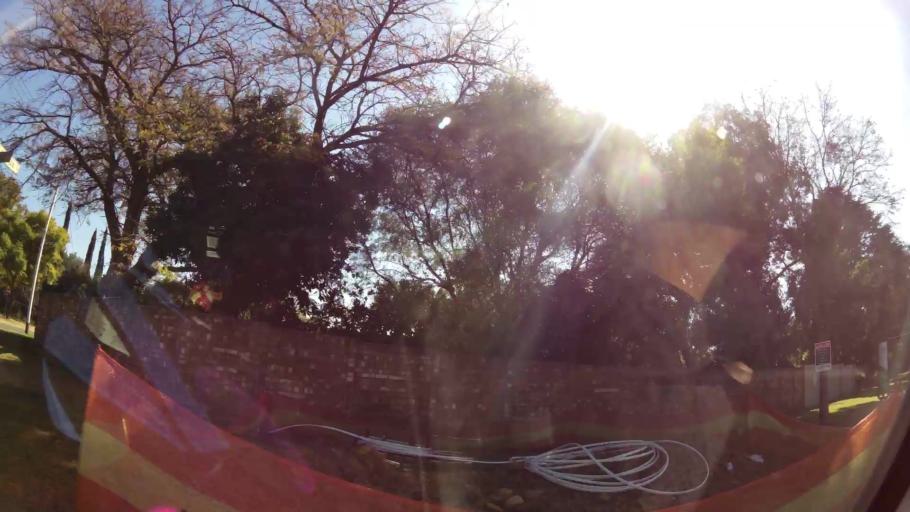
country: ZA
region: Gauteng
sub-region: City of Tshwane Metropolitan Municipality
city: Pretoria
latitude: -25.7805
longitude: 28.2653
